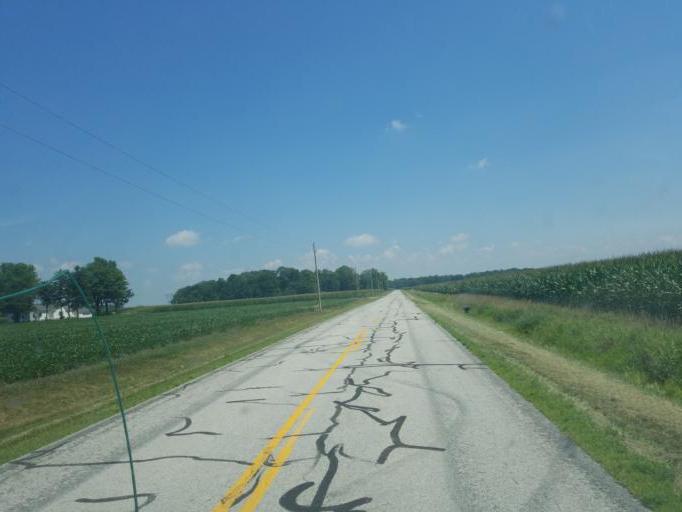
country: US
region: Ohio
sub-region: Auglaize County
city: Wapakoneta
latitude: 40.5404
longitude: -84.2461
